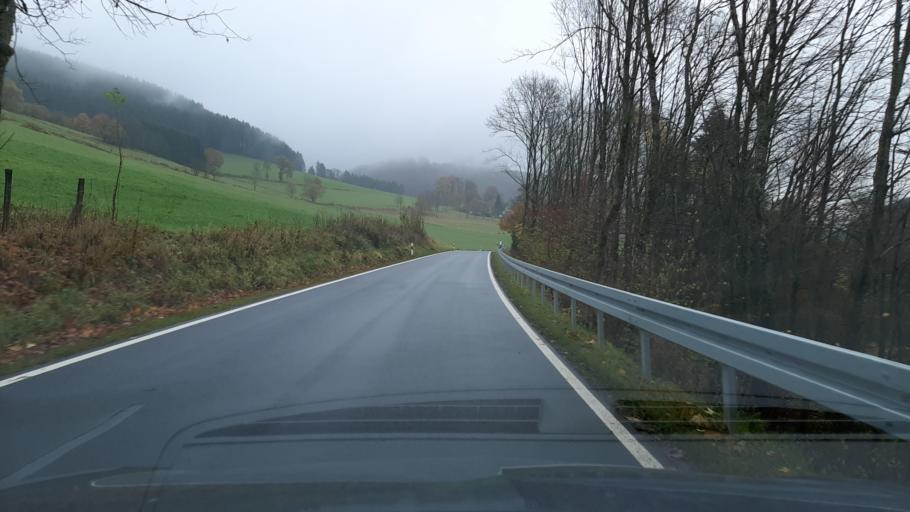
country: DE
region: North Rhine-Westphalia
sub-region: Regierungsbezirk Arnsberg
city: Bad Fredeburg
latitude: 51.1891
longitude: 8.3715
